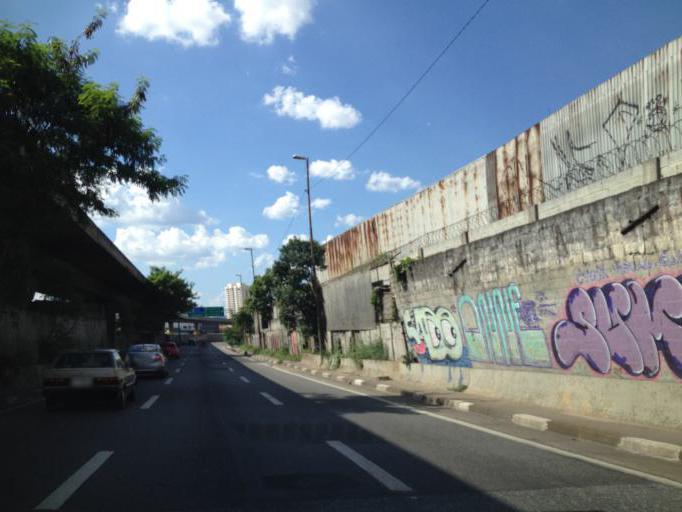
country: BR
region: Sao Paulo
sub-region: Sao Paulo
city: Sao Paulo
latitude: -23.5265
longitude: -46.5858
